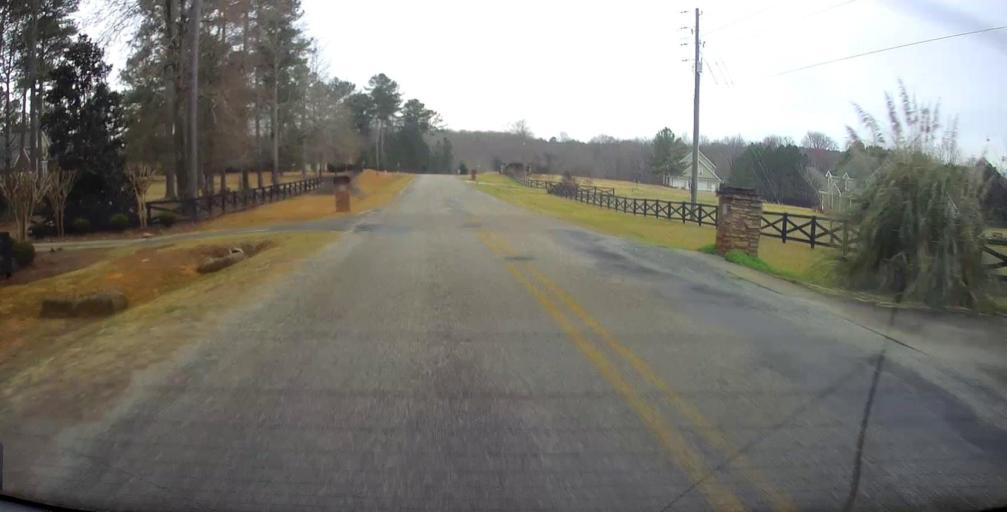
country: US
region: Georgia
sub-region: Monroe County
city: Forsyth
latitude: 33.0059
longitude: -83.8208
